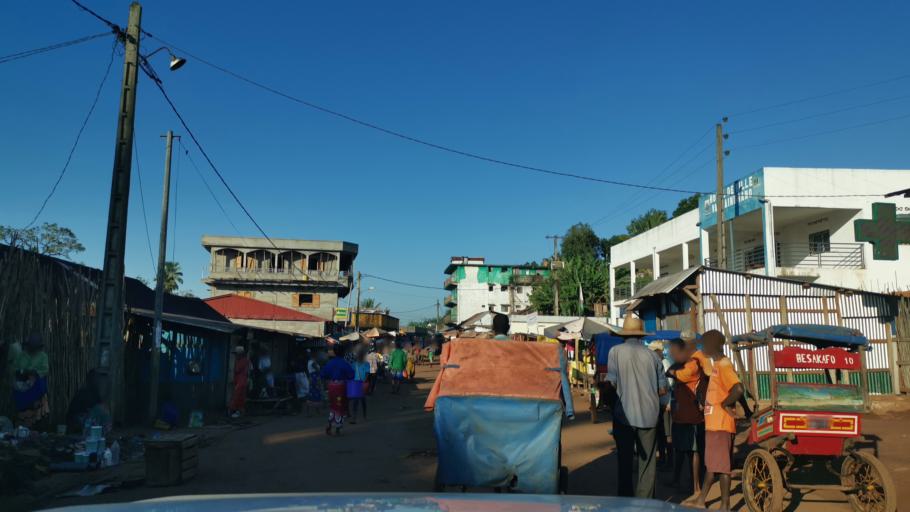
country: MG
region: Atsimo-Atsinanana
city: Vangaindrano
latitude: -23.3496
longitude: 47.6051
